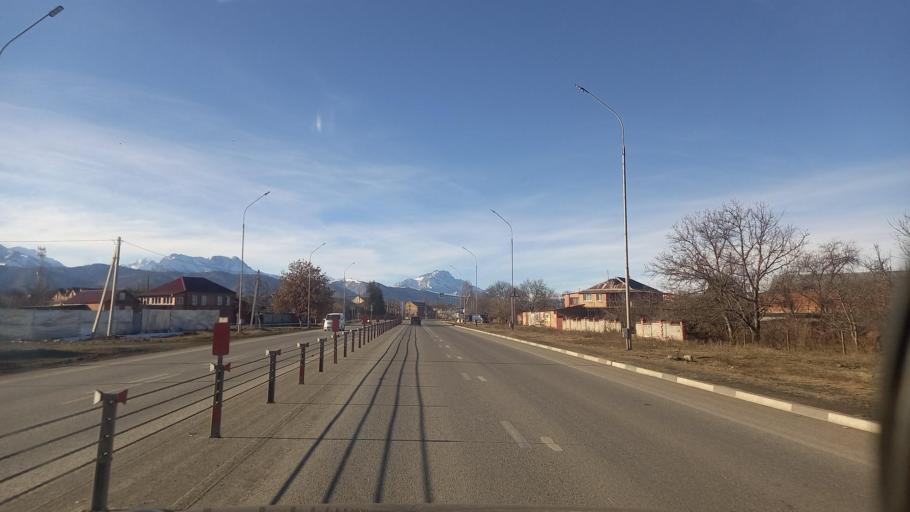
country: RU
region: North Ossetia
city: Gizel'
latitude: 43.0264
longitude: 44.5741
